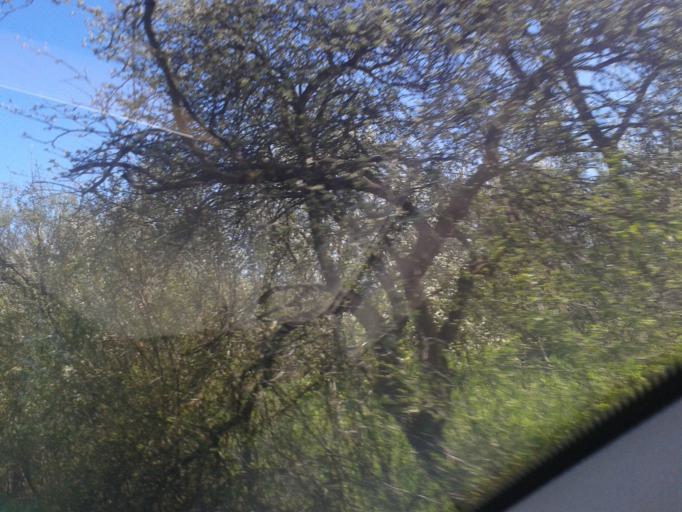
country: CZ
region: Central Bohemia
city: Revnice
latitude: 49.8940
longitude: 14.1417
